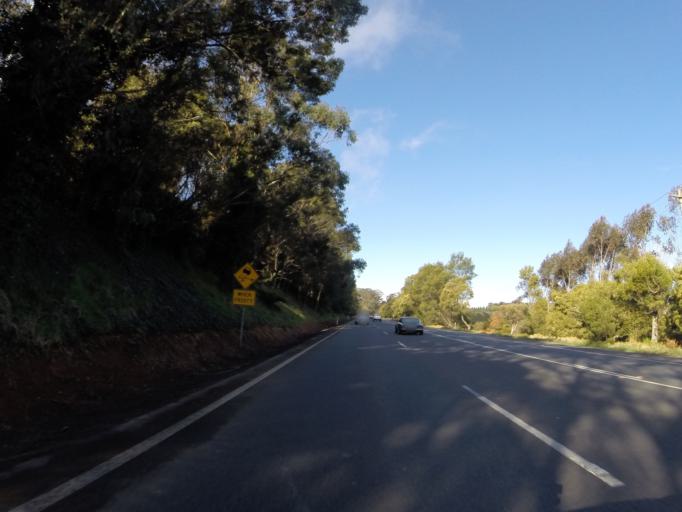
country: AU
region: New South Wales
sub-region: Shoalhaven Shire
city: Kangaroo Valley
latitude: -34.5873
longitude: 150.5507
